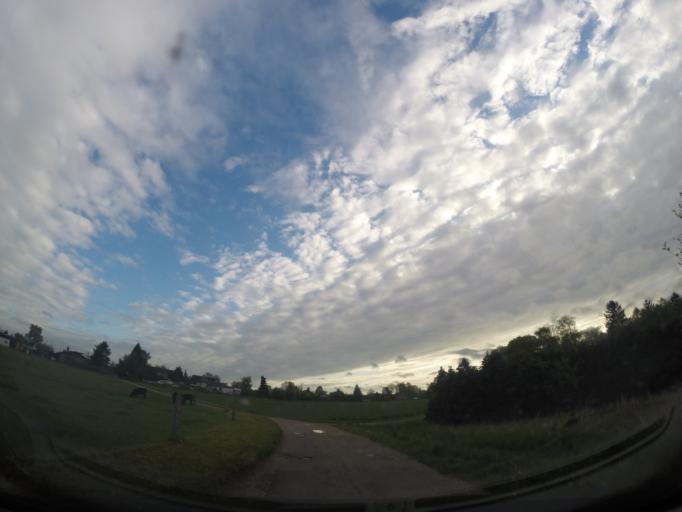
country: DK
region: Capital Region
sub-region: Hoje-Taastrup Kommune
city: Taastrup
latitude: 55.6839
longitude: 12.2578
